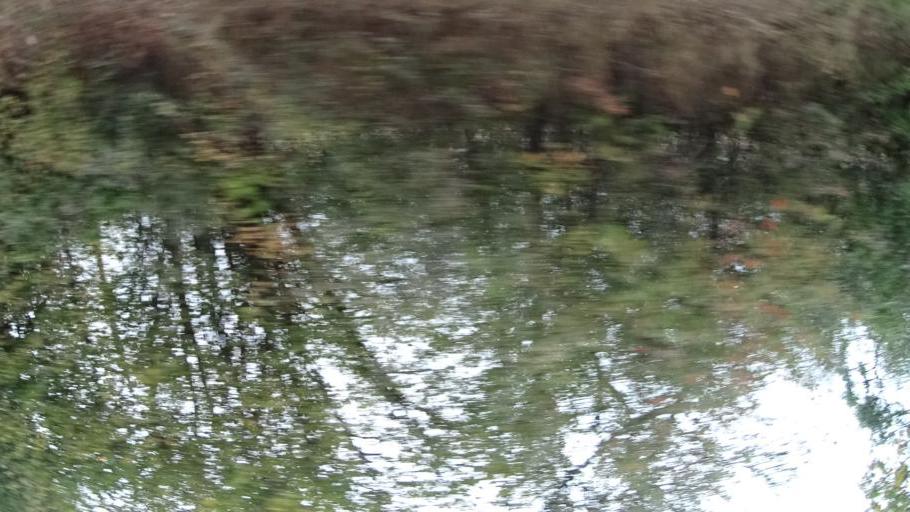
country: DE
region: Thuringia
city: Kaltenwestheim
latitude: 50.5825
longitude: 10.1264
